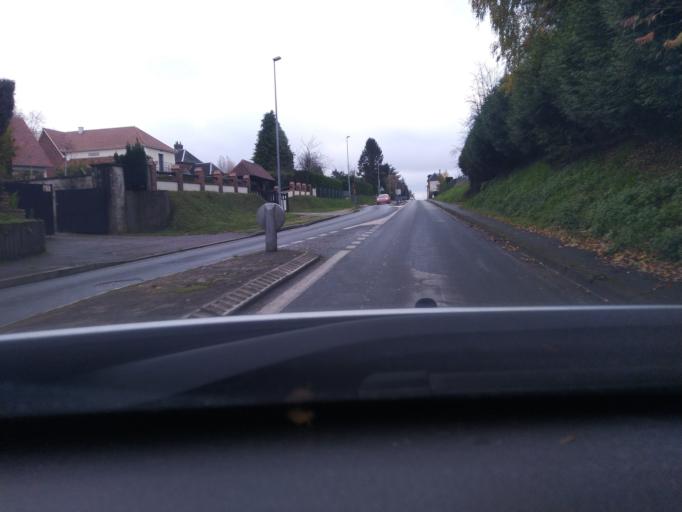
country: FR
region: Haute-Normandie
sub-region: Departement de la Seine-Maritime
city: La Vaupaliere
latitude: 49.4903
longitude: 1.0006
